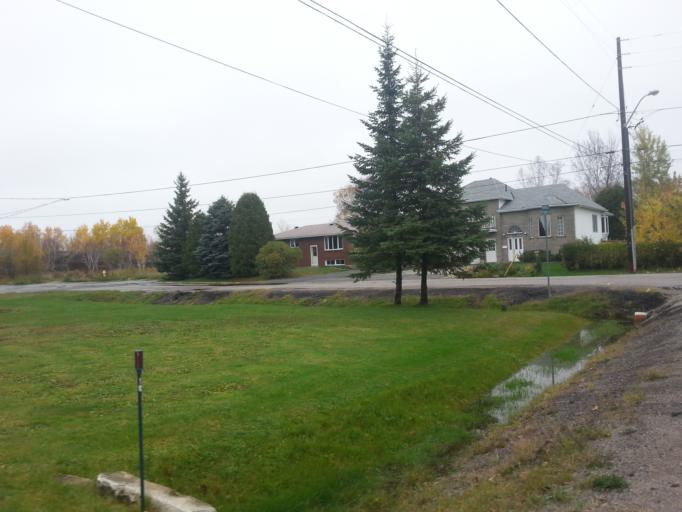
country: CA
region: Ontario
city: Greater Sudbury
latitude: 46.5440
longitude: -81.0981
